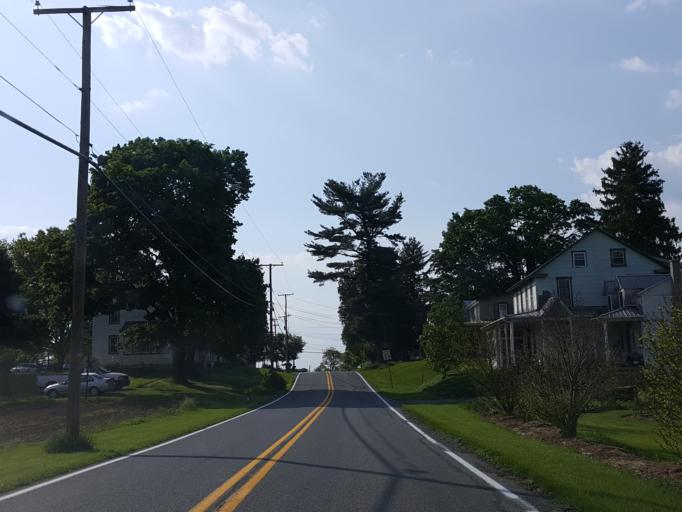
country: US
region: Pennsylvania
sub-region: Lebanon County
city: Campbelltown
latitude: 40.2417
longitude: -76.5931
